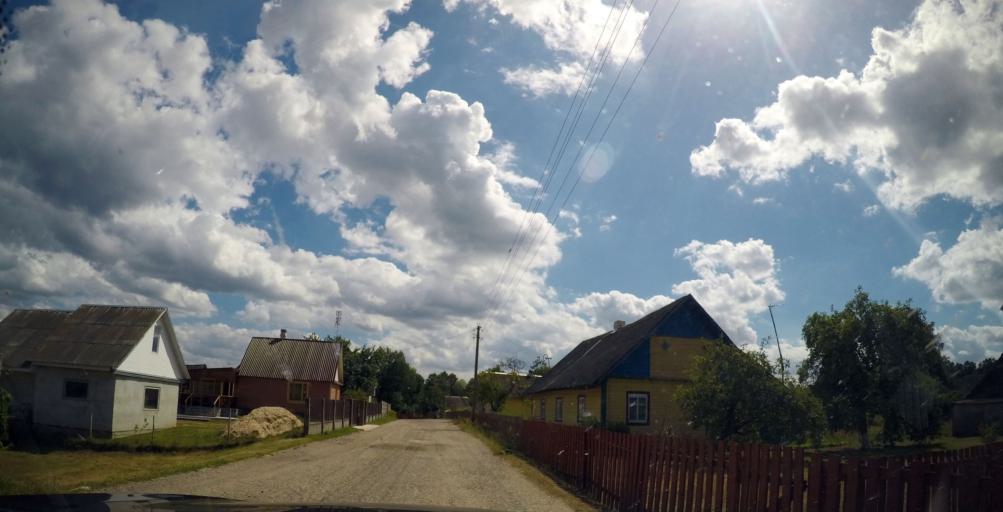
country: BY
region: Grodnenskaya
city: Skidal'
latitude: 53.8218
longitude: 24.2438
